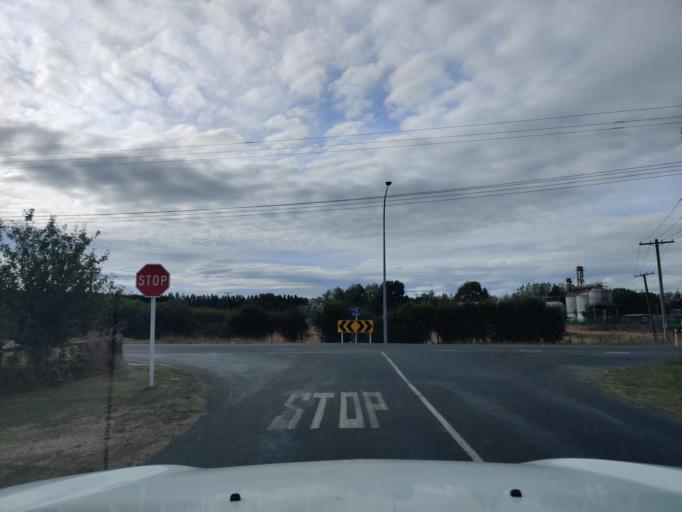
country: NZ
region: Waikato
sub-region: Waipa District
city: Cambridge
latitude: -37.7833
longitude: 175.4240
